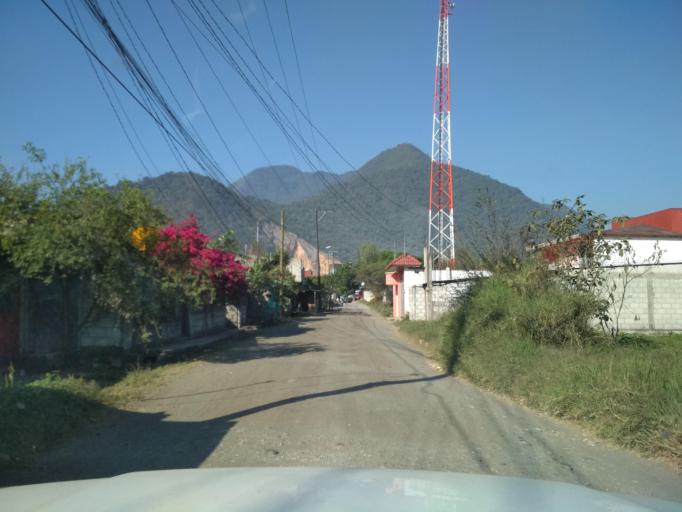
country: MX
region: Veracruz
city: Jalapilla
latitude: 18.8238
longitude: -97.0827
